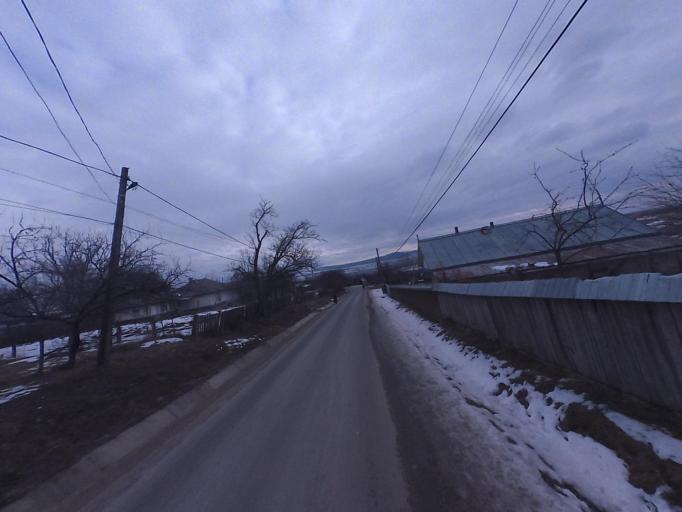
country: RO
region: Iasi
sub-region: Comuna Tibanesti
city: Glodenii Gandului
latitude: 46.9792
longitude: 27.2963
